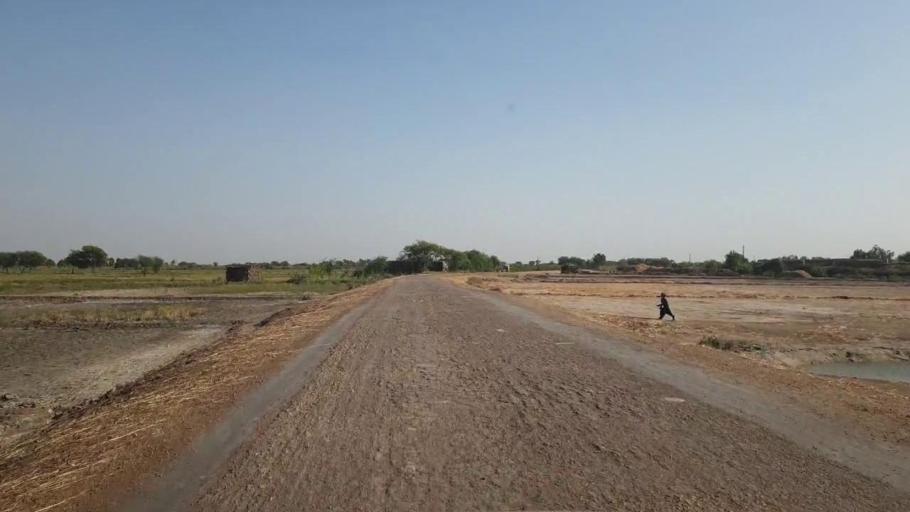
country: PK
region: Sindh
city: Matli
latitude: 25.0386
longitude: 68.7275
